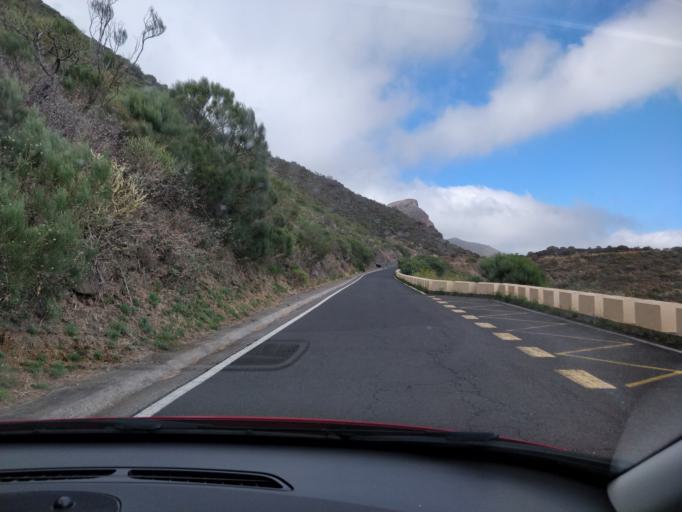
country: ES
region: Canary Islands
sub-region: Provincia de Santa Cruz de Tenerife
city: Santiago del Teide
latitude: 28.3154
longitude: -16.8480
